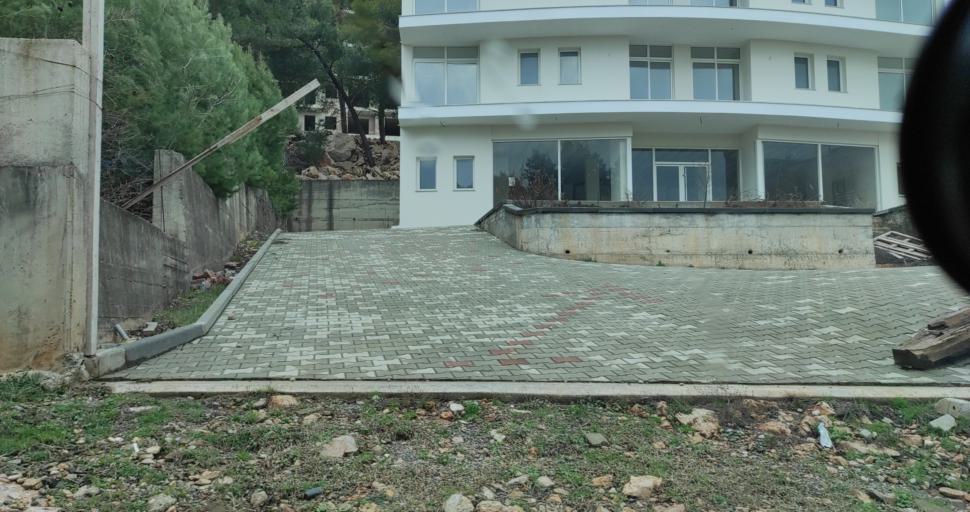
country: AL
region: Lezhe
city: Shengjin
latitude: 41.8126
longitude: 19.5779
